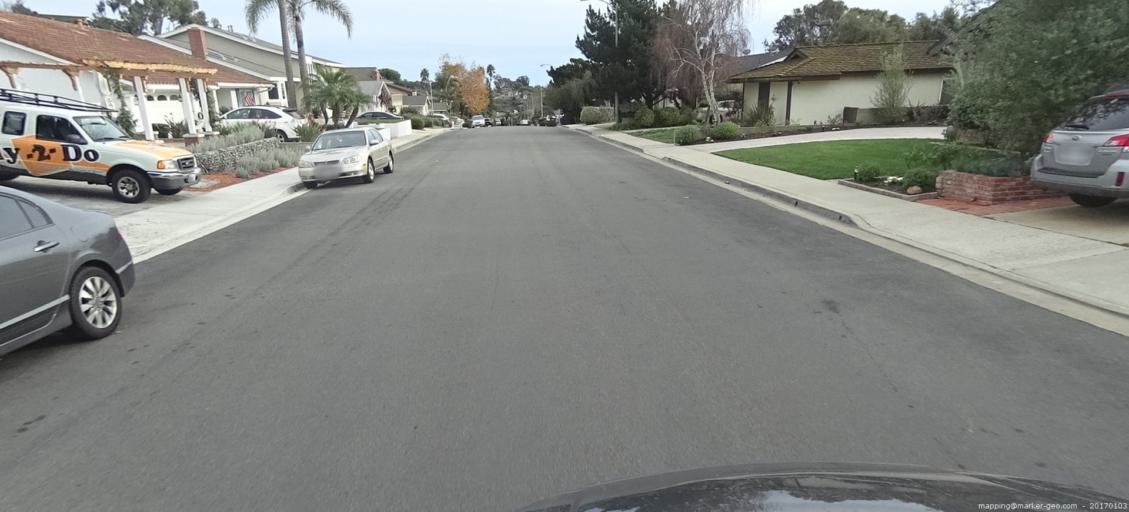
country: US
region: California
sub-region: Orange County
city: Dana Point
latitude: 33.4800
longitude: -117.6935
